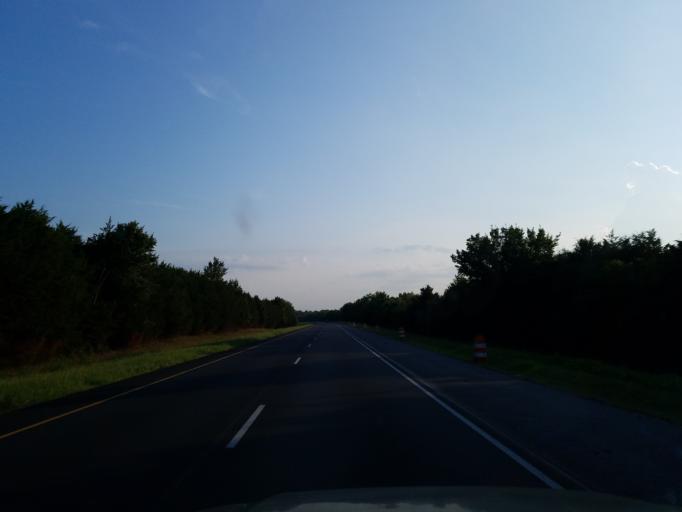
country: US
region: Alabama
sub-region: Sumter County
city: Livingston
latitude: 32.6501
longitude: -88.1927
